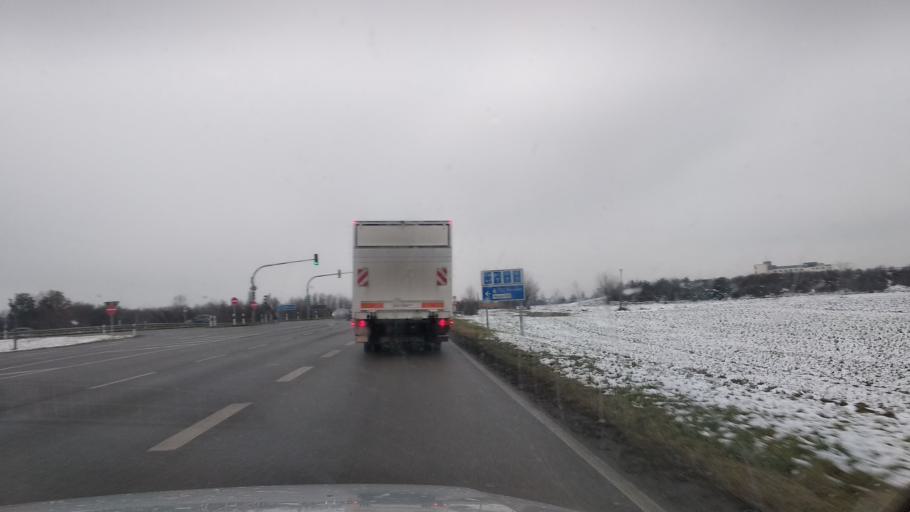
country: DE
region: Bavaria
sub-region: Upper Bavaria
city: Feldkirchen
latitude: 48.1452
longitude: 11.7455
